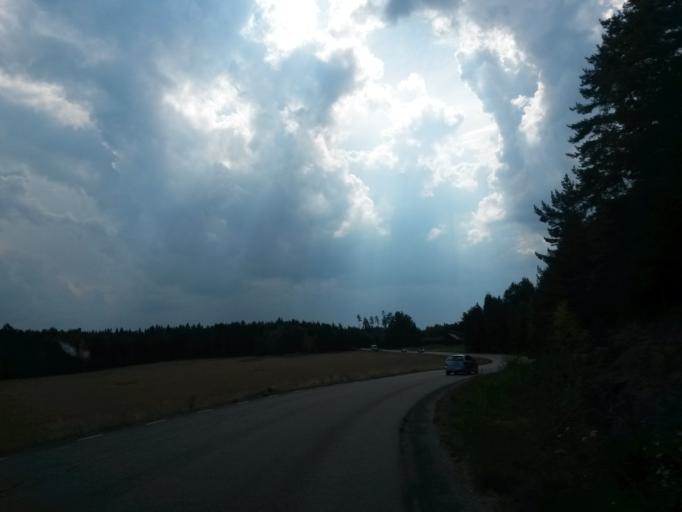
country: SE
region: Vaestra Goetaland
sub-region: Lidkopings Kommun
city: Lidkoping
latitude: 58.6143
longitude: 13.1231
